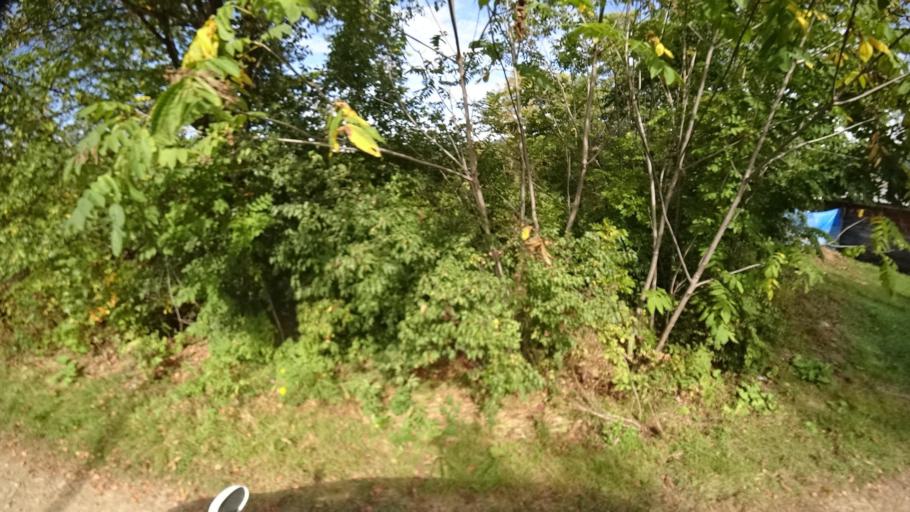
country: RU
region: Primorskiy
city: Yakovlevka
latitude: 44.3961
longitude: 133.6005
